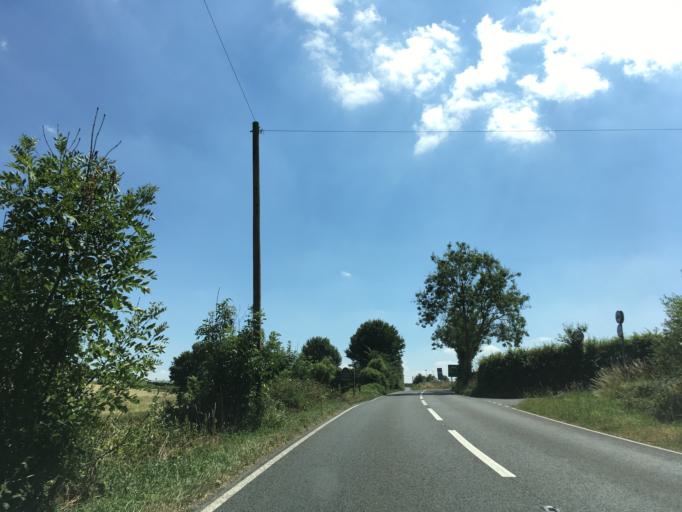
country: GB
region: England
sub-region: Gloucestershire
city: Chalford
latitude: 51.7172
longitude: -2.1342
